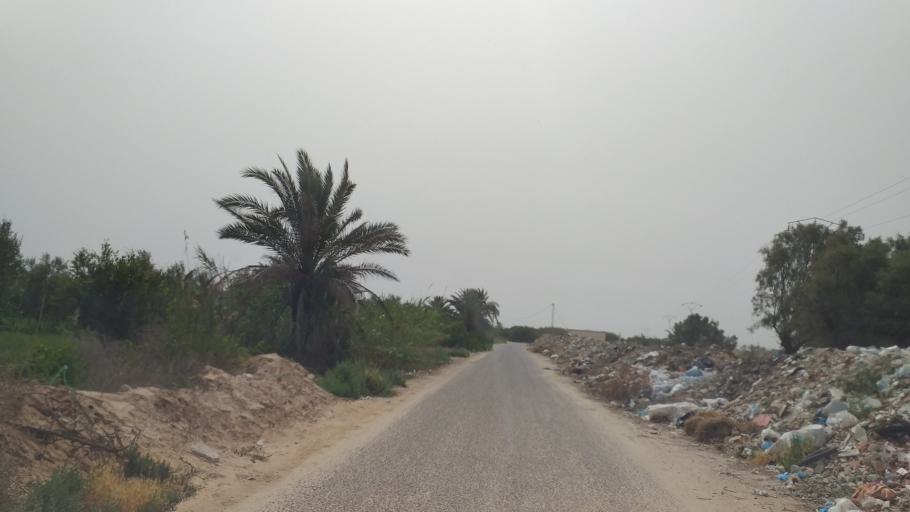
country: TN
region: Qabis
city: Gabes
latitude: 33.9463
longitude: 10.0495
